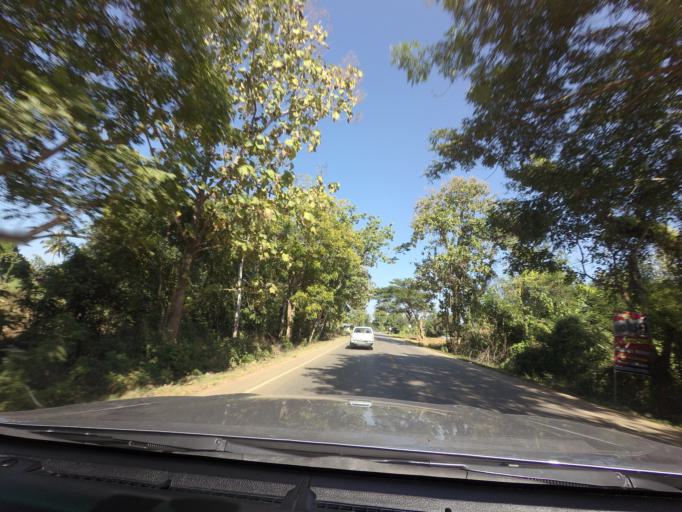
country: TH
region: Sukhothai
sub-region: Amphoe Si Satchanalai
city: Si Satchanalai
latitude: 17.6732
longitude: 99.6947
